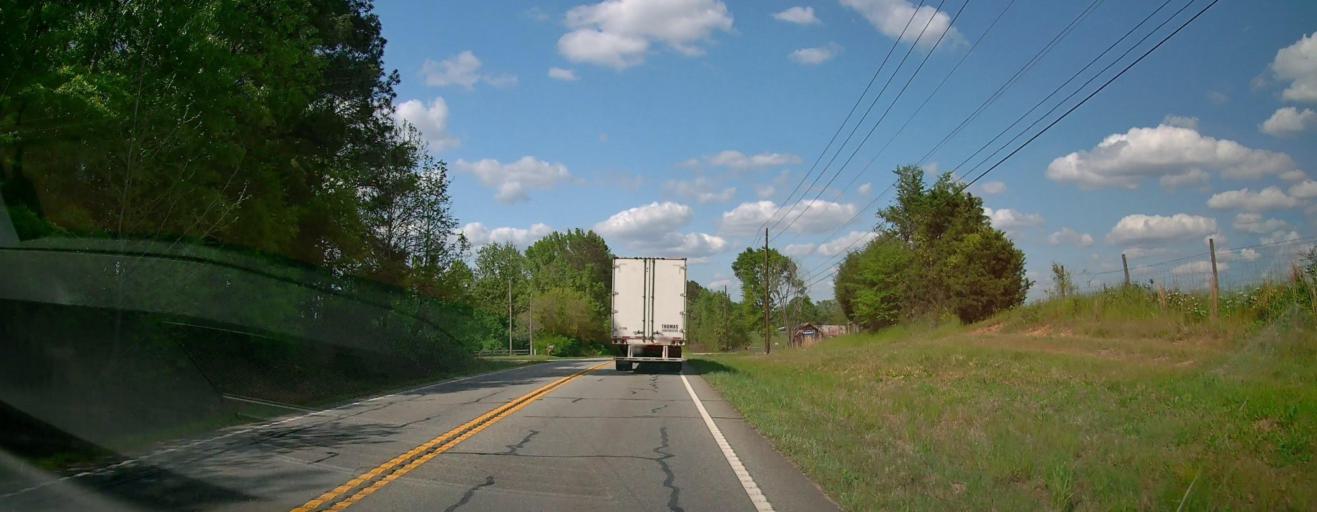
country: US
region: Georgia
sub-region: Greene County
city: Greensboro
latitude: 33.5235
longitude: -83.2220
